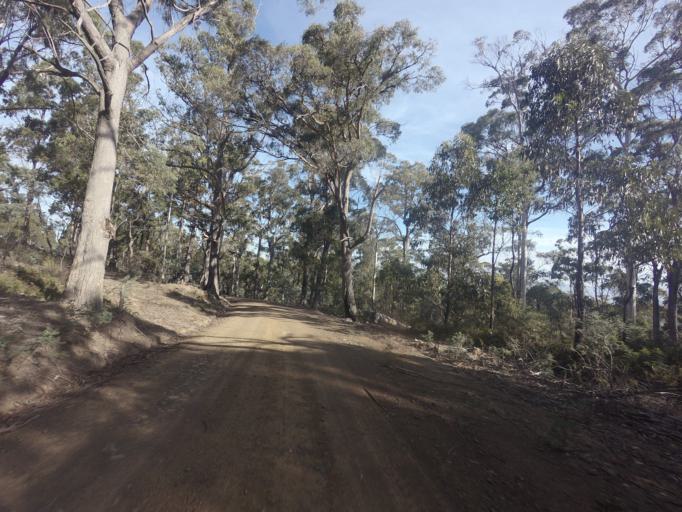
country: AU
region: Tasmania
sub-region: Sorell
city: Sorell
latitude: -42.5161
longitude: 147.4710
